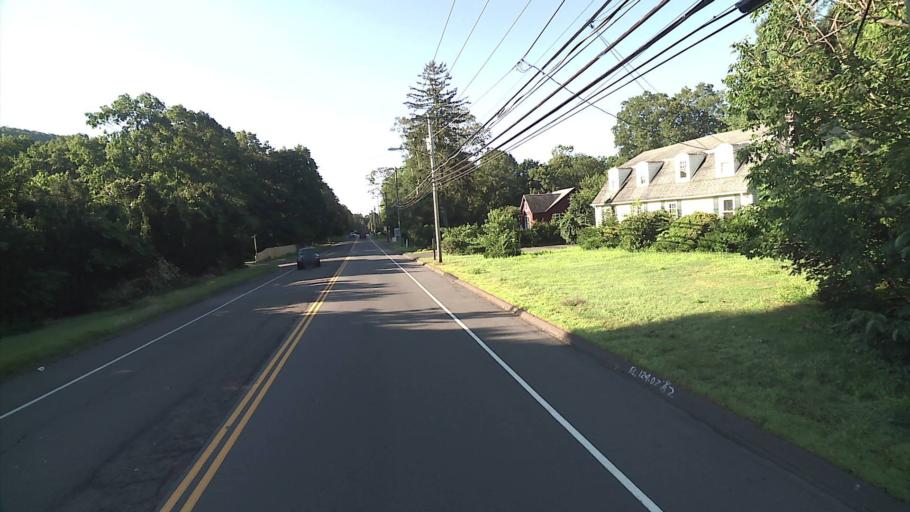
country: US
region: Connecticut
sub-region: New Haven County
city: Hamden
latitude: 41.4313
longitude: -72.9075
